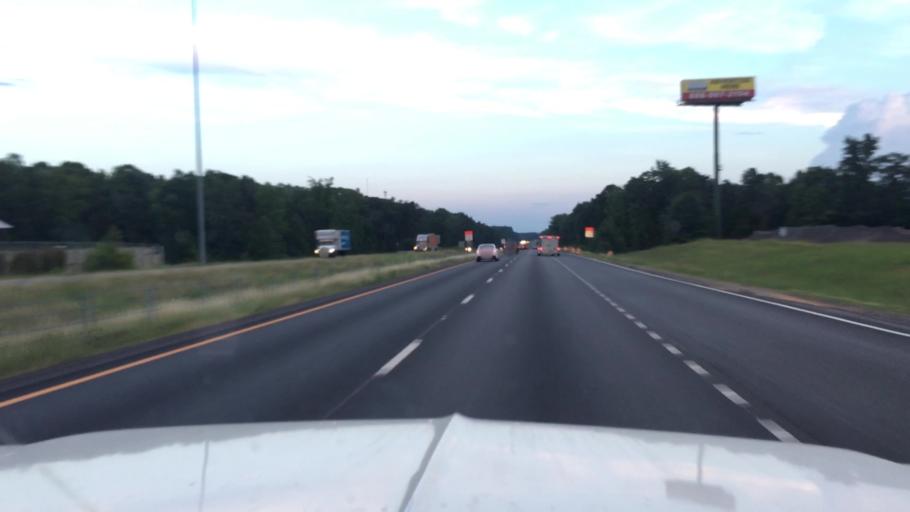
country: US
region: Alabama
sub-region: Chilton County
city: Jemison
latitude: 32.9768
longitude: -86.6862
